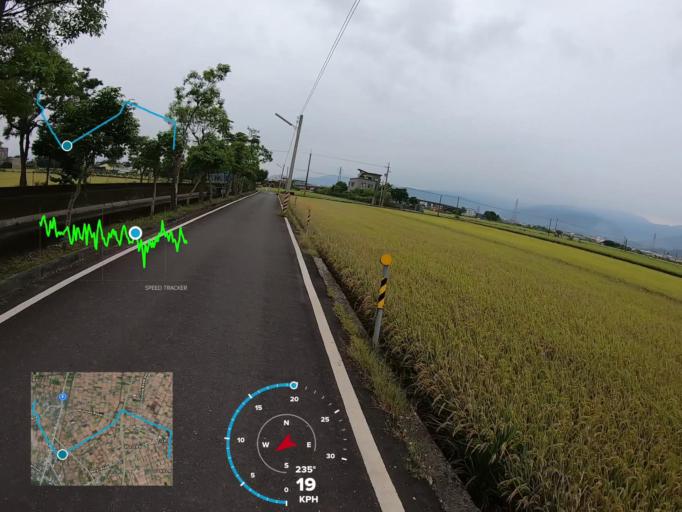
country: TW
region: Taiwan
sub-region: Yilan
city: Yilan
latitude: 24.7772
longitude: 121.7683
